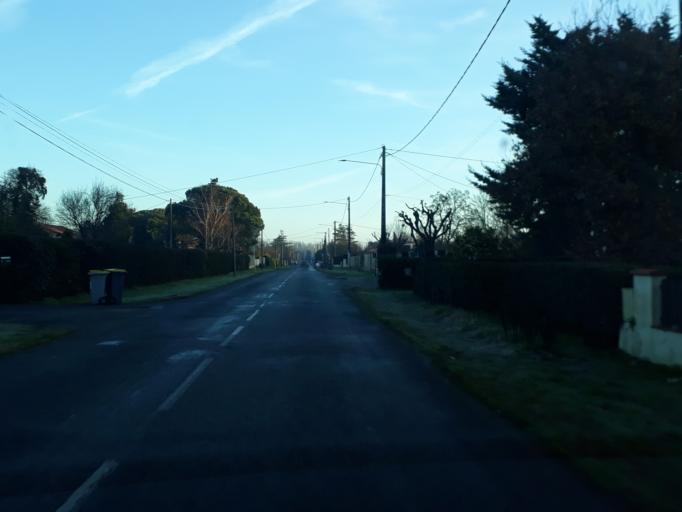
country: FR
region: Midi-Pyrenees
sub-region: Departement de la Haute-Garonne
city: Longages
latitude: 43.3430
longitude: 1.2332
